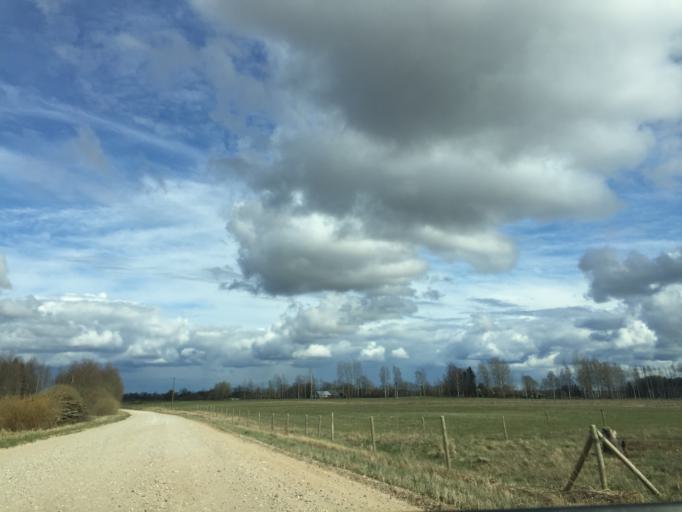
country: LV
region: Limbazu Rajons
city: Limbazi
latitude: 57.6167
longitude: 24.7008
